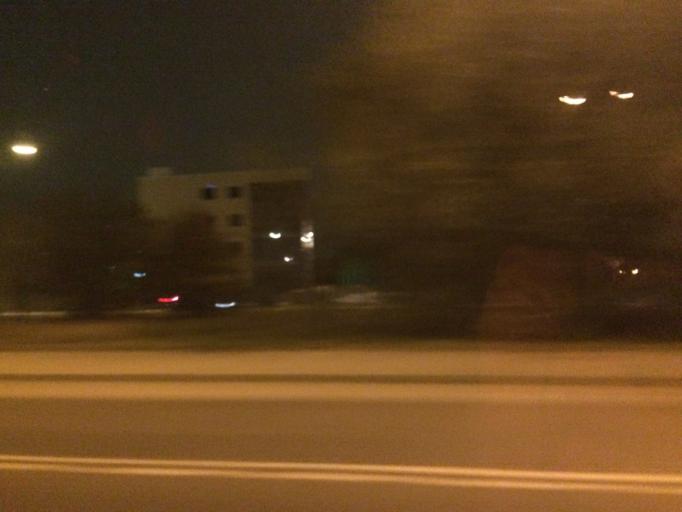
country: KZ
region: Astana Qalasy
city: Astana
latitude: 51.1871
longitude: 71.4501
